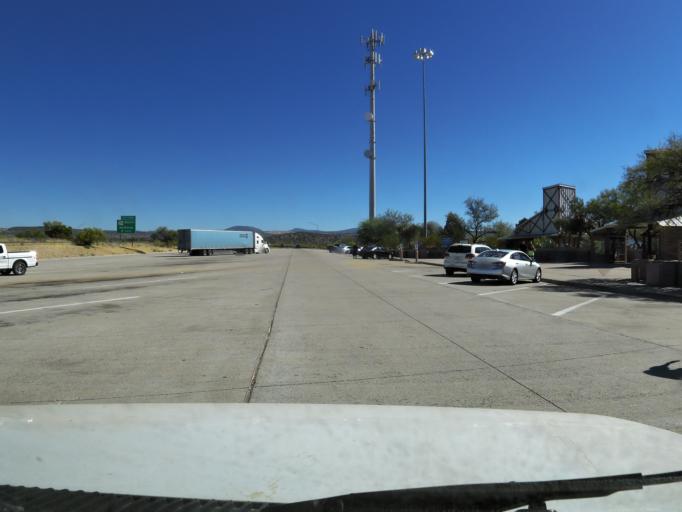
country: US
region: Arizona
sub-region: Yavapai County
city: Lake Montezuma
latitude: 34.6725
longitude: -111.7732
